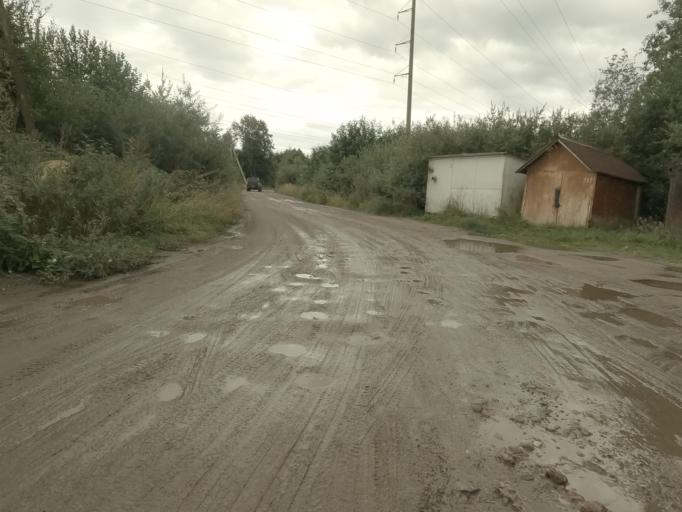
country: RU
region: Leningrad
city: Kirovsk
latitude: 59.8913
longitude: 31.0025
